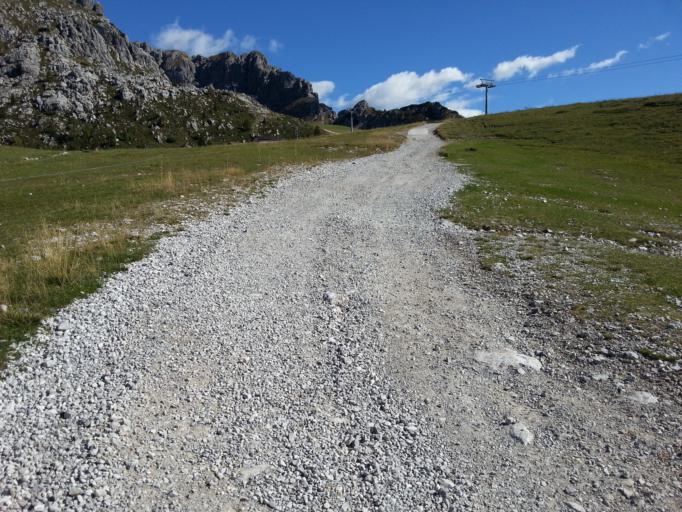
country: IT
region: Lombardy
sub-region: Provincia di Lecco
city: Moggio
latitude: 45.9601
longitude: 9.4973
